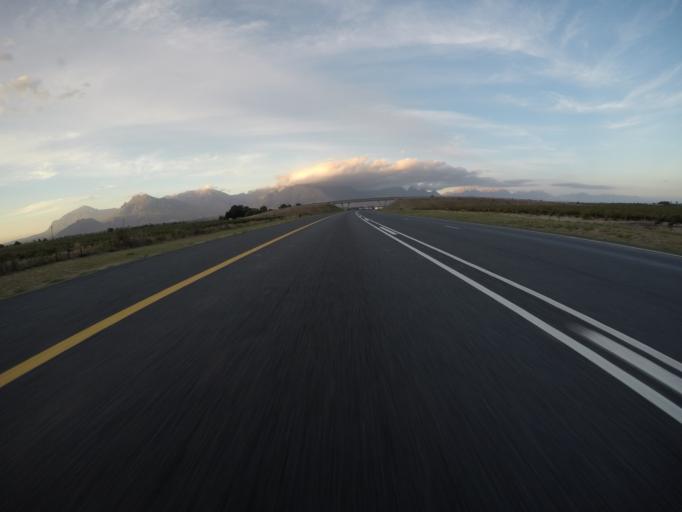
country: ZA
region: Western Cape
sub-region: Cape Winelands District Municipality
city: Worcester
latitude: -33.6545
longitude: 19.2901
